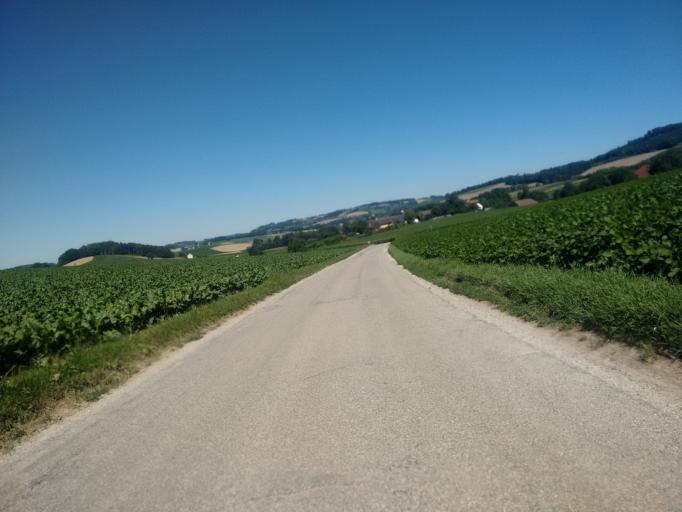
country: AT
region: Upper Austria
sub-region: Wels-Land
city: Buchkirchen
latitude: 48.2189
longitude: 13.9975
